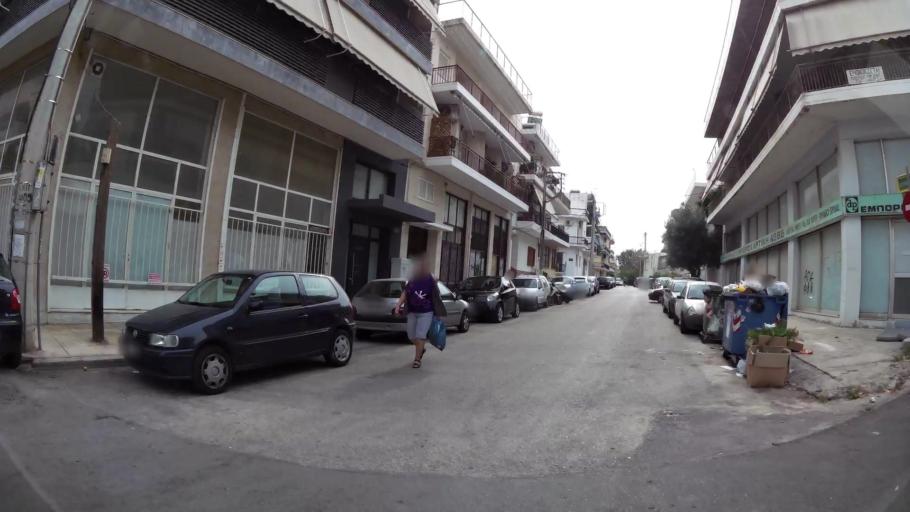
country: GR
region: Attica
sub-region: Nomarchia Athinas
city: Agios Dimitrios
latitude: 37.9302
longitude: 23.7432
